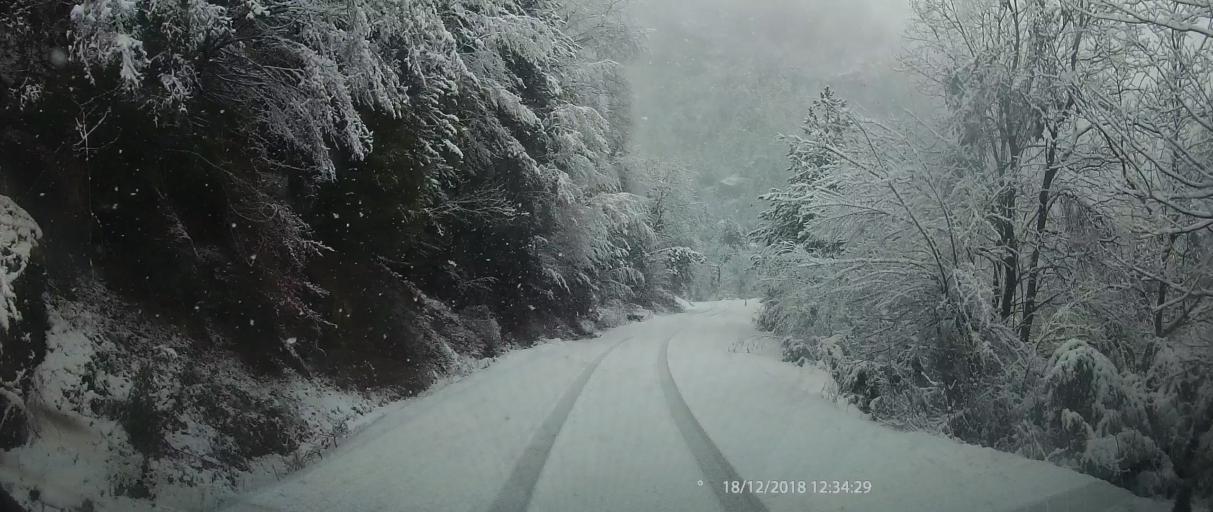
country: GR
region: Central Macedonia
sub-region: Nomos Pierias
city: Litochoro
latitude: 40.0849
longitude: 22.4069
